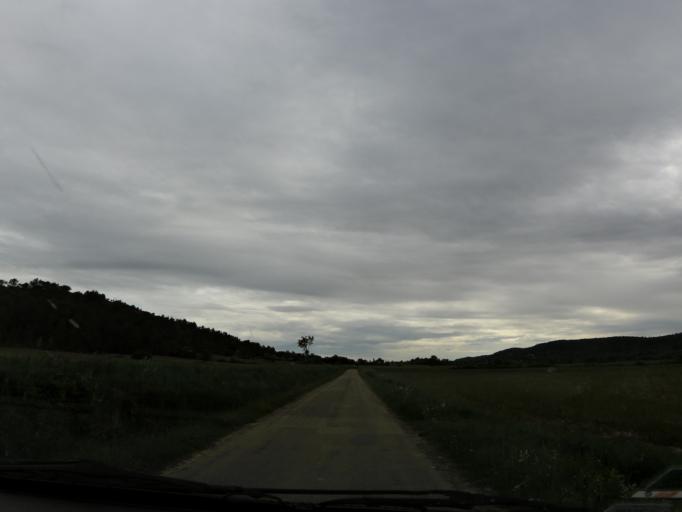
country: FR
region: Languedoc-Roussillon
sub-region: Departement du Gard
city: Quissac
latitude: 43.8670
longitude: 4.0270
